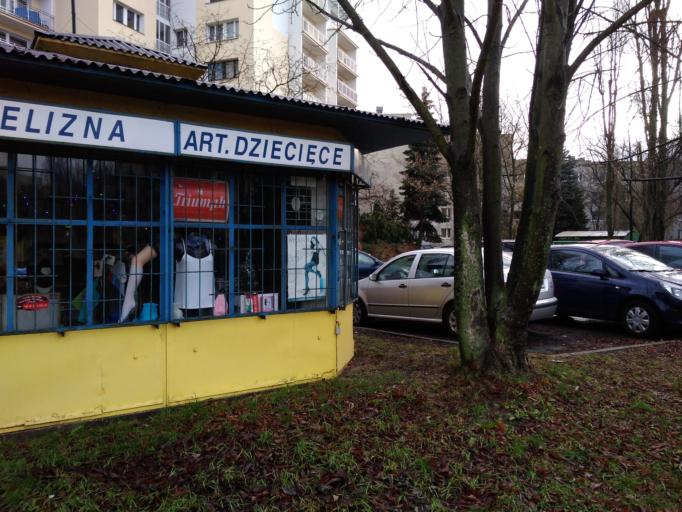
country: PL
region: Masovian Voivodeship
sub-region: Warszawa
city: Ursynow
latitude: 52.1579
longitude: 21.0368
